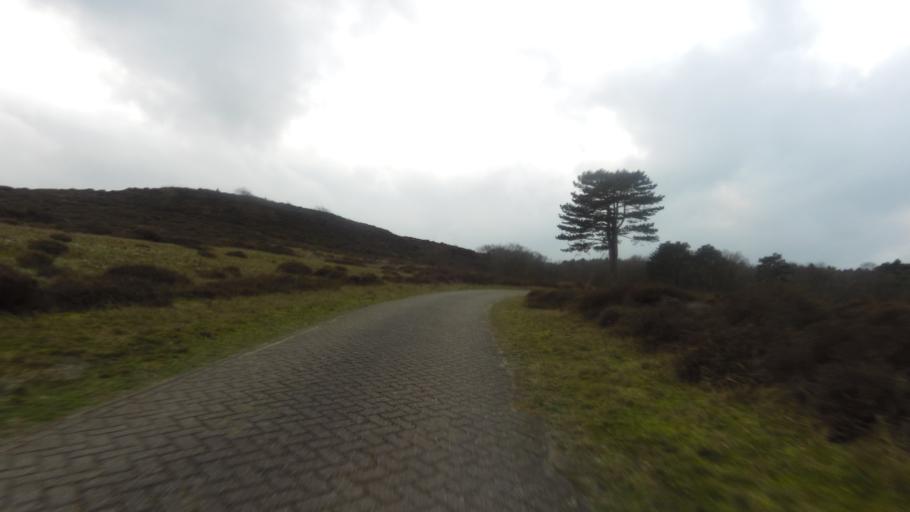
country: NL
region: North Holland
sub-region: Gemeente Bergen
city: Egmond aan Zee
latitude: 52.6715
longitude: 4.6519
